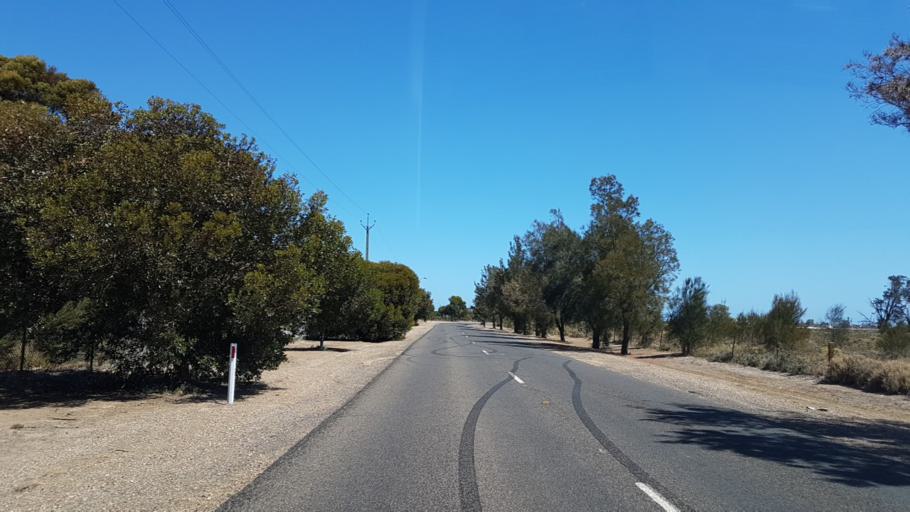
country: AU
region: South Australia
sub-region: Playford
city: Virginia
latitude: -34.7351
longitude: 138.5477
